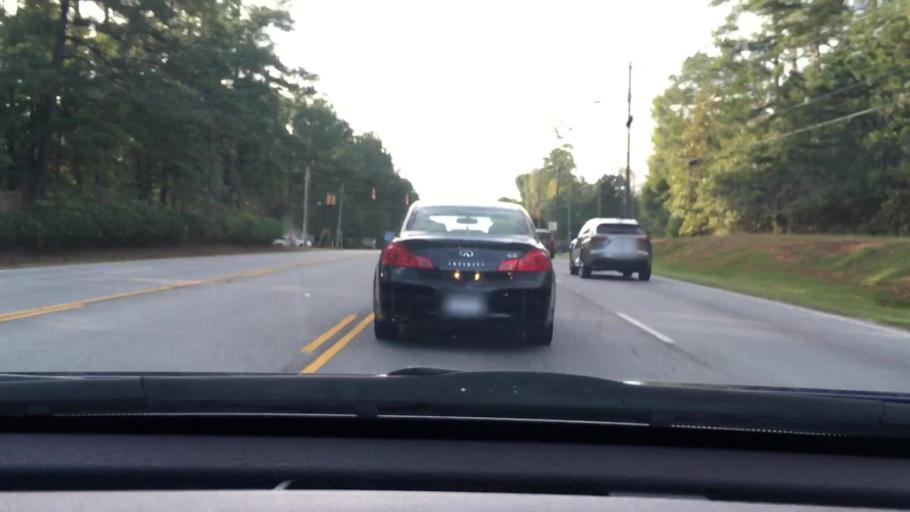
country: US
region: South Carolina
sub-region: Lexington County
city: Seven Oaks
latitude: 34.0833
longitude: -81.1373
